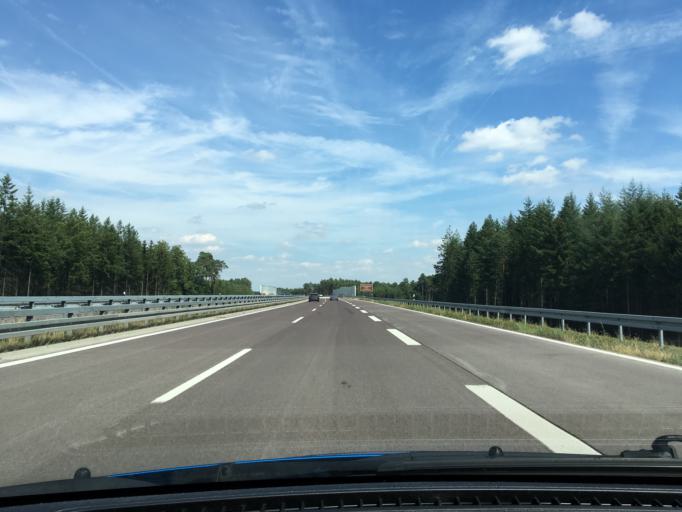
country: DE
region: Mecklenburg-Vorpommern
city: Gross Laasch
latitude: 53.3856
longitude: 11.5278
